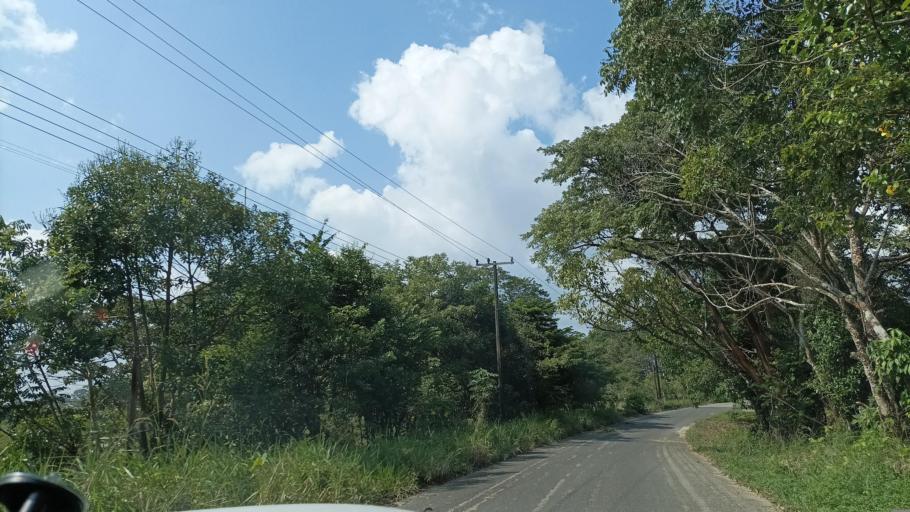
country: MX
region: Veracruz
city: Las Choapas
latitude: 17.7514
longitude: -94.1118
